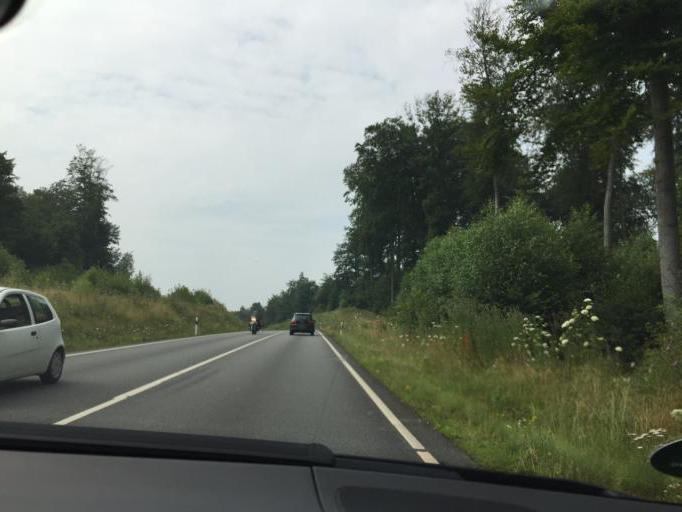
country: DE
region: Rheinland-Pfalz
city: Bonefeld
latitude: 50.5176
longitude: 7.4852
